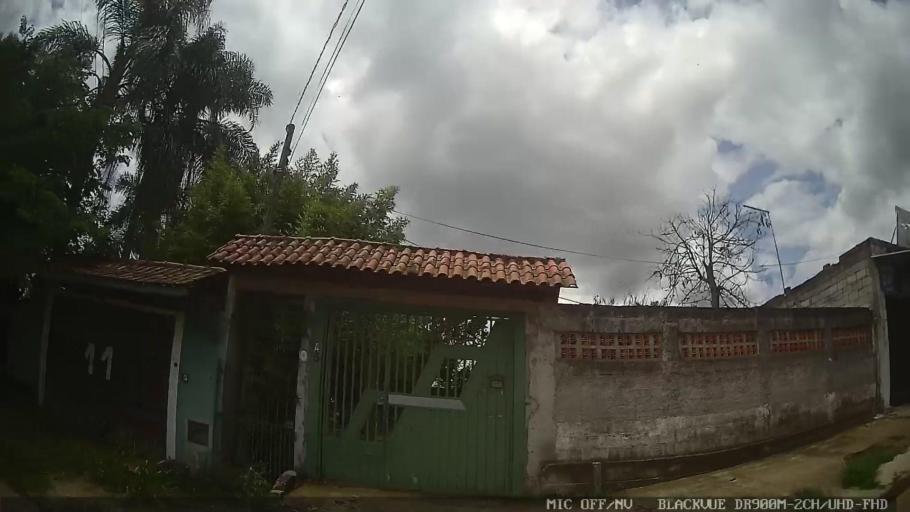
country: BR
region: Sao Paulo
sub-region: Suzano
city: Suzano
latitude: -23.6013
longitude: -46.2503
